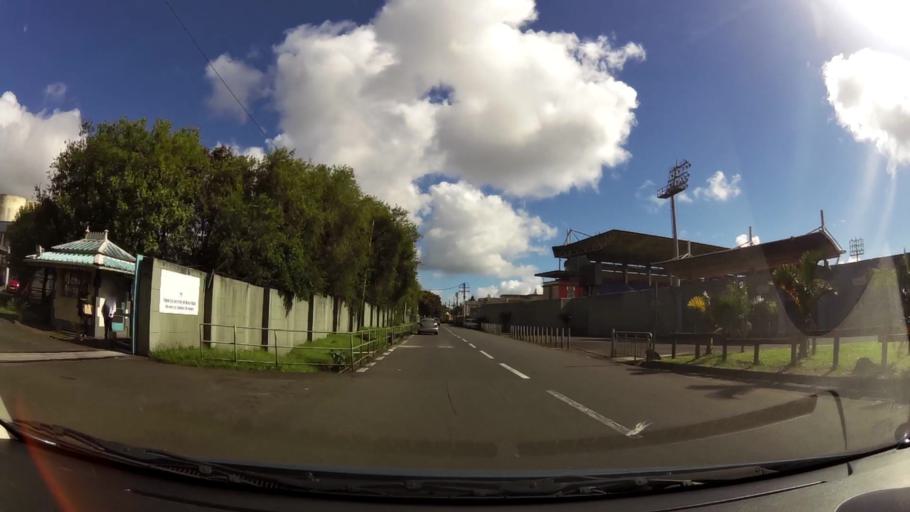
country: MU
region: Plaines Wilhems
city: Curepipe
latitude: -20.3219
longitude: 57.5305
